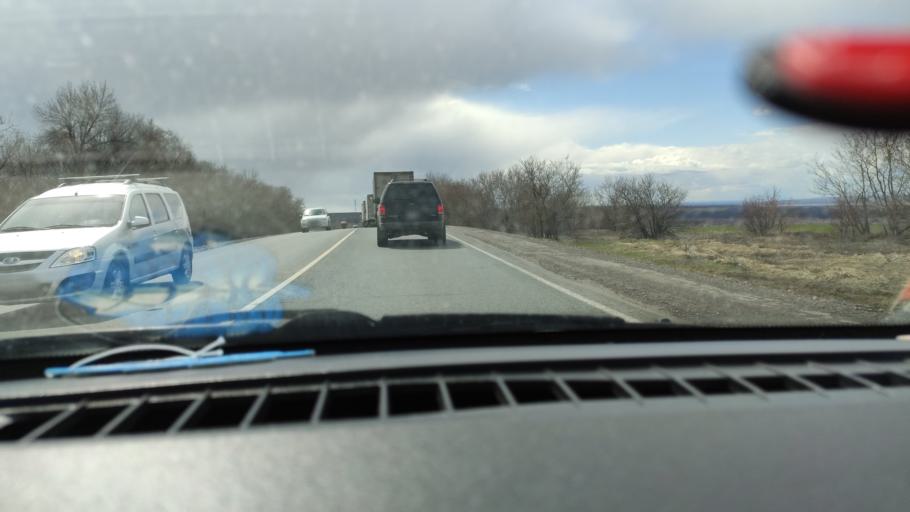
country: RU
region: Samara
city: Zhigulevsk
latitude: 53.3060
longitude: 49.3505
